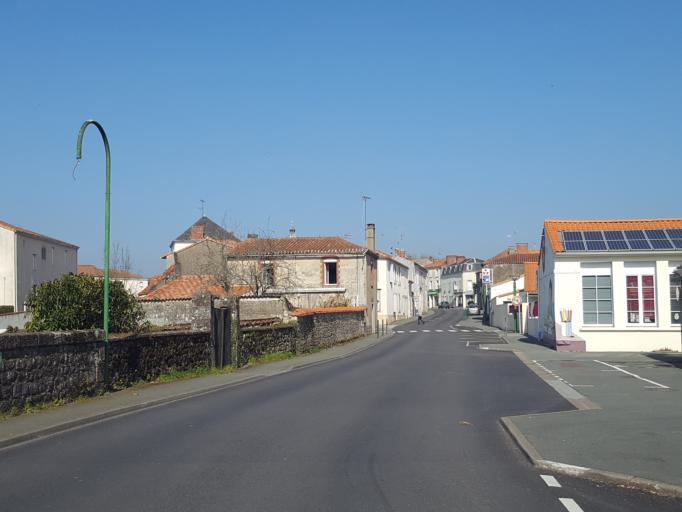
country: FR
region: Pays de la Loire
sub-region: Departement de la Vendee
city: La Chaize-le-Vicomte
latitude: 46.6710
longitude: -1.2913
